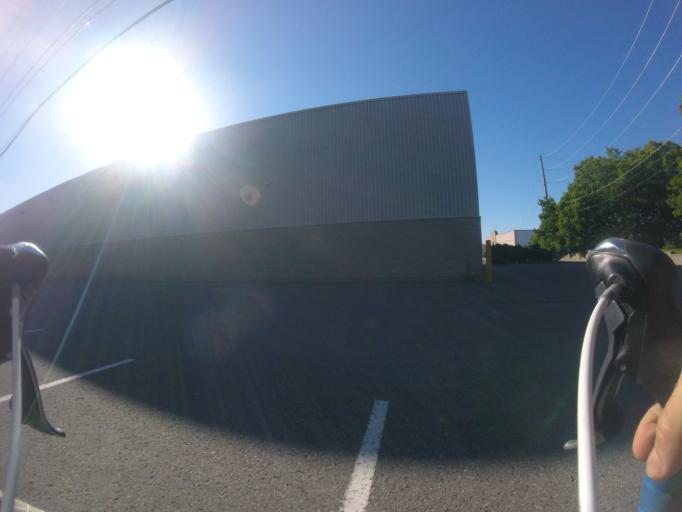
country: CA
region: Ontario
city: Ottawa
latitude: 45.3324
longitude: -75.7254
